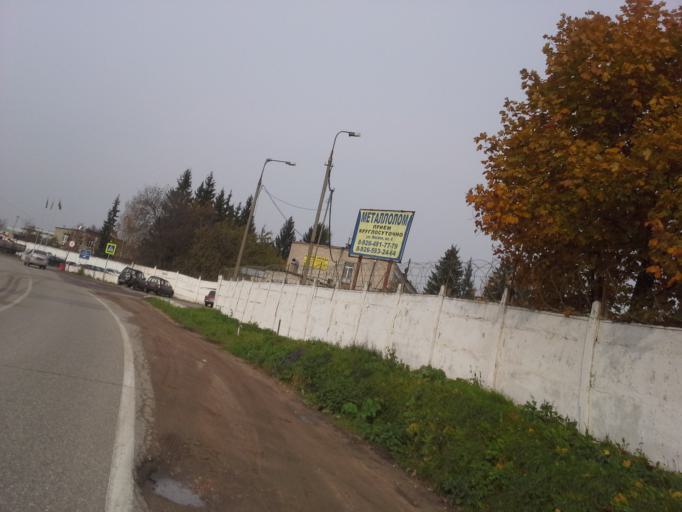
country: RU
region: Moskovskaya
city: Bol'shiye Vyazemy
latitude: 55.6360
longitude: 37.0042
